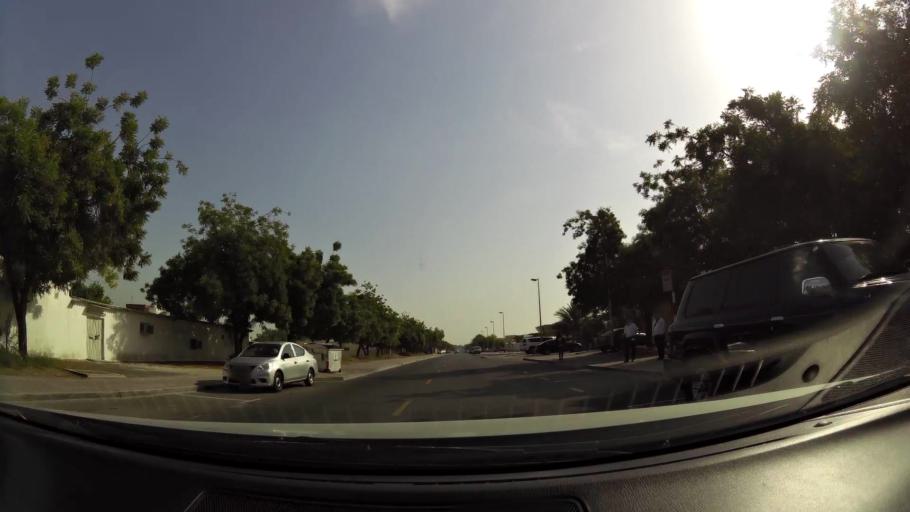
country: AE
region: Ash Shariqah
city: Sharjah
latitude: 25.2173
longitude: 55.3943
